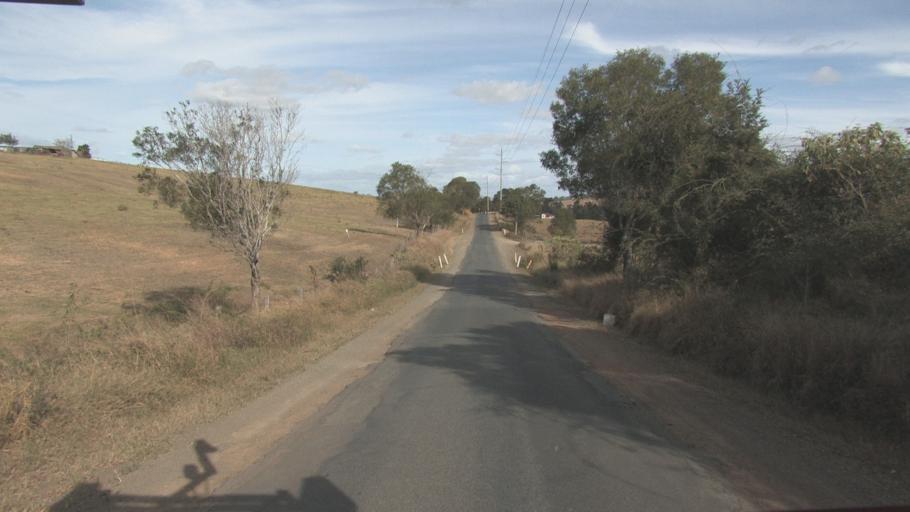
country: AU
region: Queensland
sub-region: Logan
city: Cedar Vale
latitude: -27.9072
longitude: 153.0136
